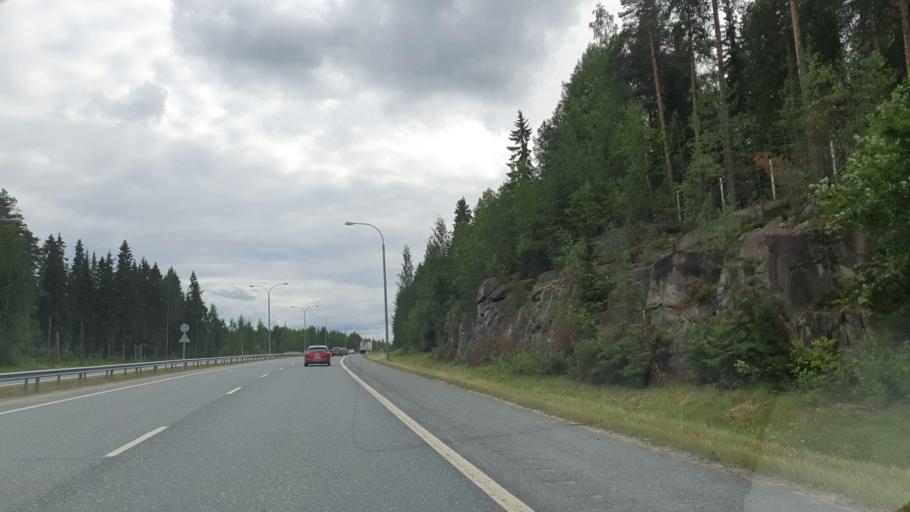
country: FI
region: Northern Savo
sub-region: Ylae-Savo
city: Iisalmi
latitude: 63.5566
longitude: 27.2563
